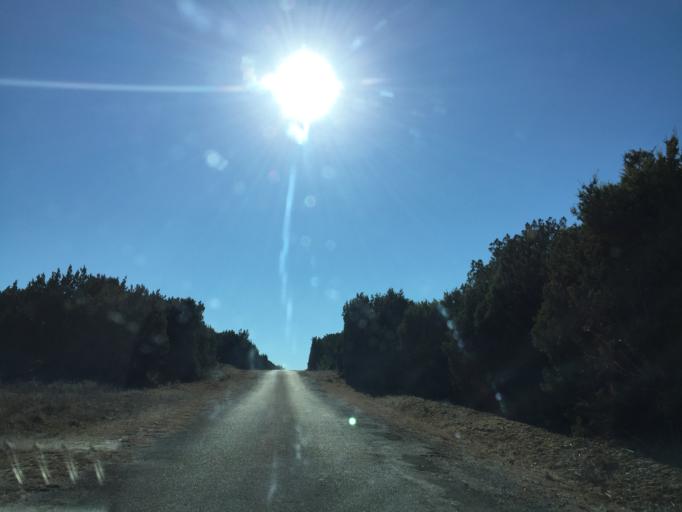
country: US
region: Texas
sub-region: Lampasas County
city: Lampasas
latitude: 30.9416
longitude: -98.1669
